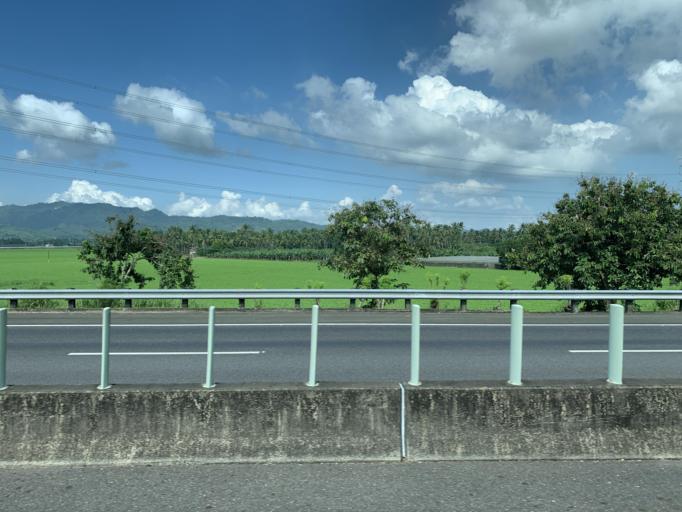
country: TW
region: Taiwan
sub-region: Pingtung
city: Pingtung
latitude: 22.8324
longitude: 120.4919
